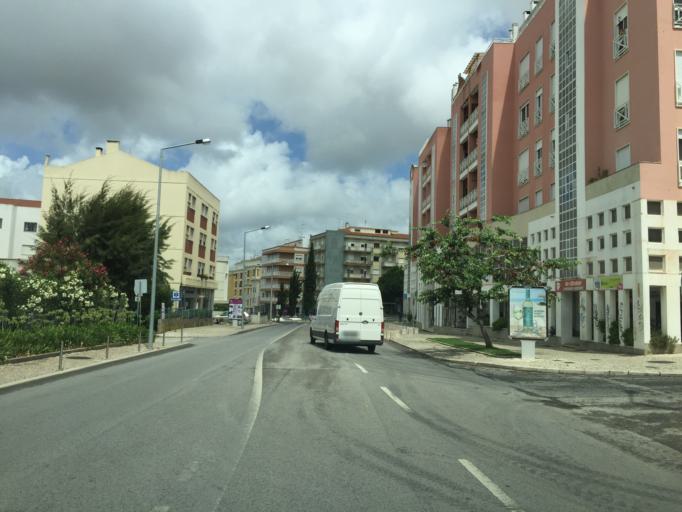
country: PT
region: Lisbon
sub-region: Torres Vedras
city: Torres Vedras
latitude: 39.0862
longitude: -9.2565
